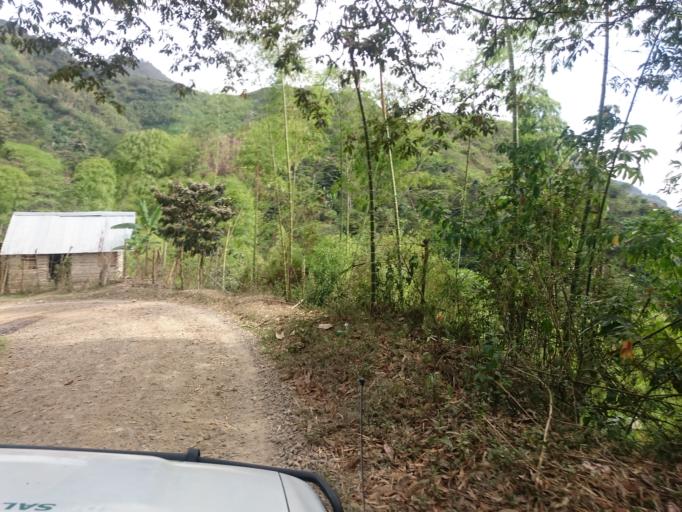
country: CO
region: Cauca
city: Suarez
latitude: 2.9332
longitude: -76.7189
